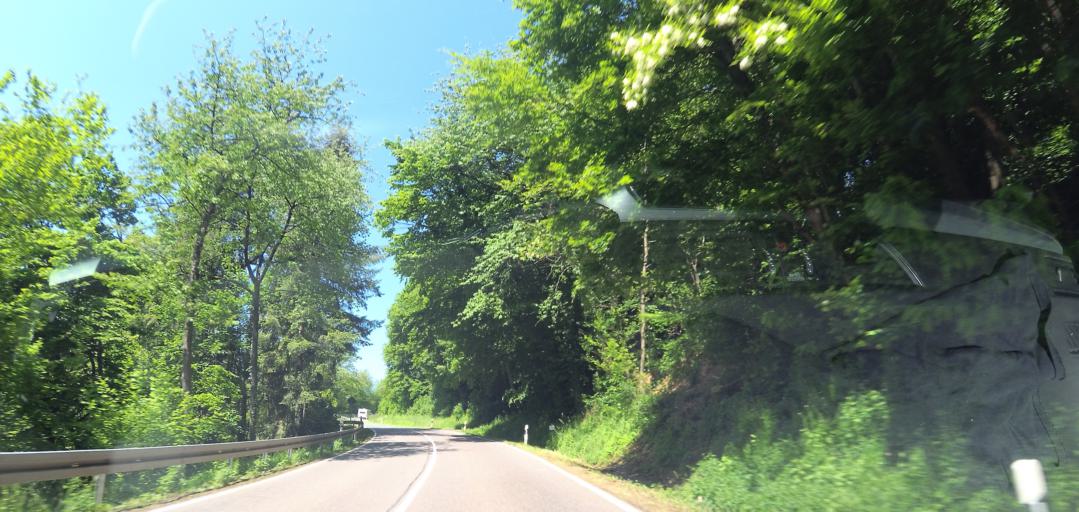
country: DE
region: Saarland
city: Losheim
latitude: 49.4573
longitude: 6.7287
